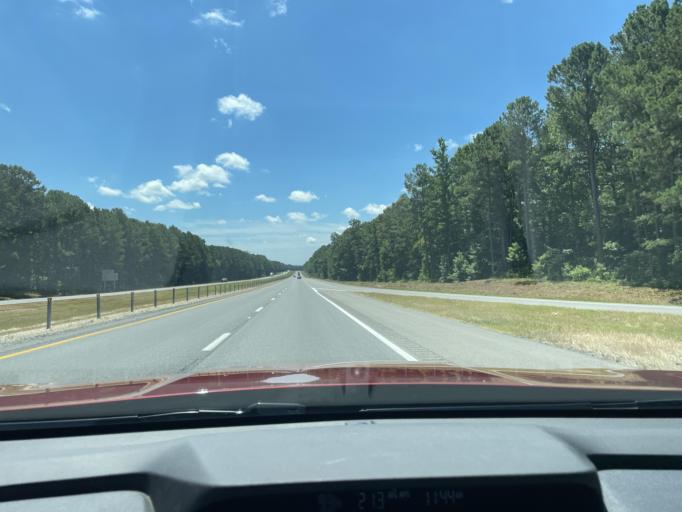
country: US
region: Arkansas
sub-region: Jefferson County
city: White Hall
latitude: 34.3057
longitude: -92.1384
